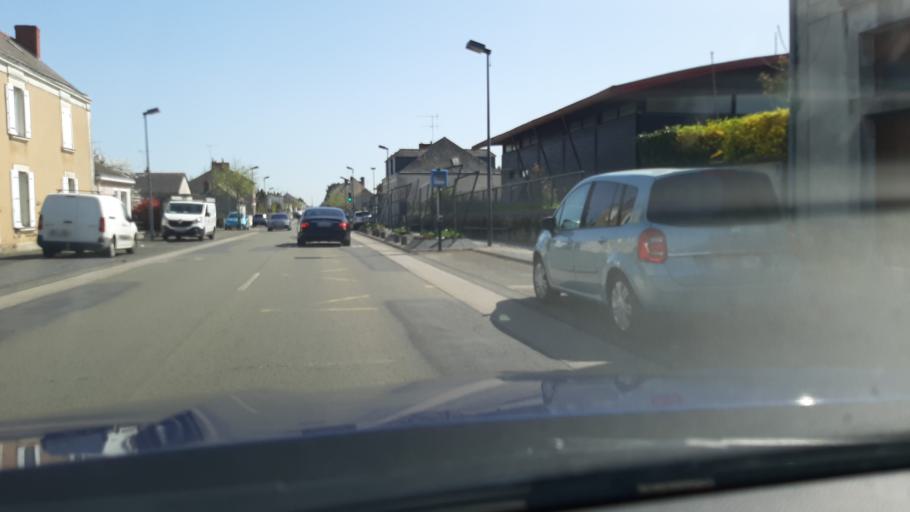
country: FR
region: Pays de la Loire
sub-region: Departement de Maine-et-Loire
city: Les Ponts-de-Ce
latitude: 47.4467
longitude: -0.5070
